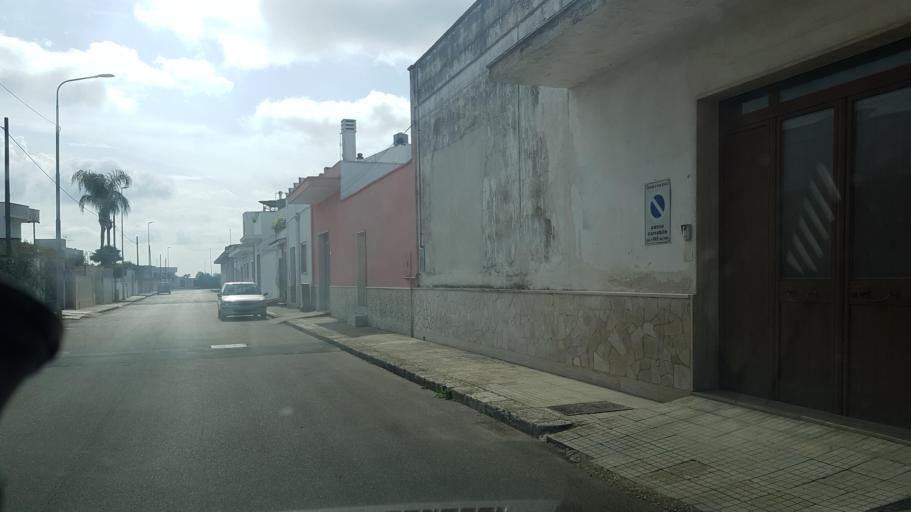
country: IT
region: Apulia
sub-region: Provincia di Brindisi
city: San Donaci
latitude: 40.4496
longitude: 17.9297
